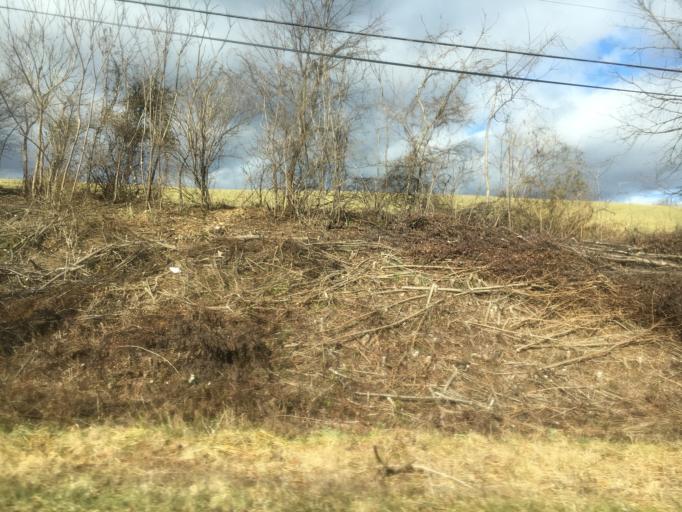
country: US
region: Pennsylvania
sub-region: Lehigh County
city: Laurys Station
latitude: 40.7031
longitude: -75.5715
